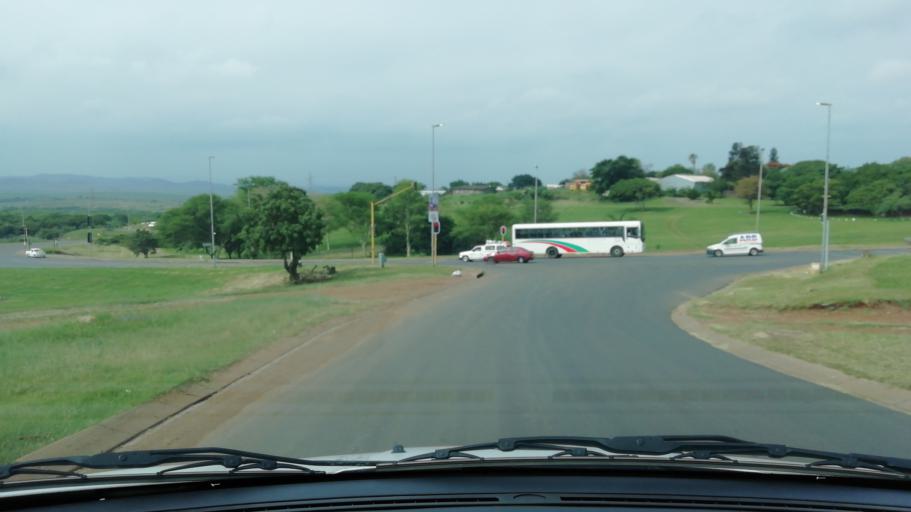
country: ZA
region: KwaZulu-Natal
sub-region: uThungulu District Municipality
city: Empangeni
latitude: -28.7433
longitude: 31.8825
